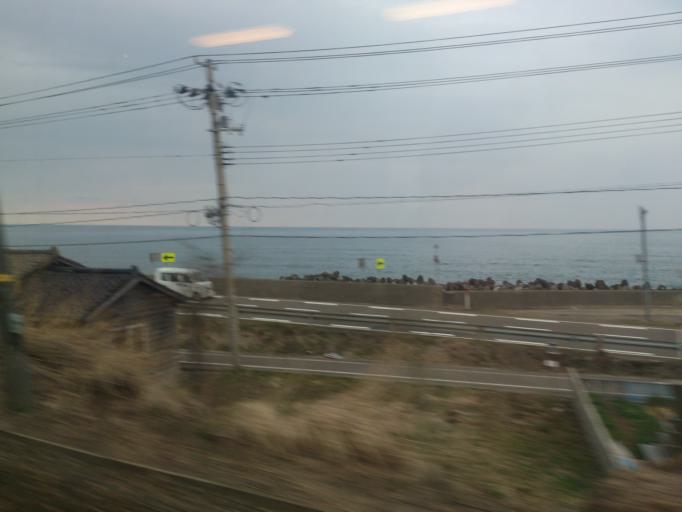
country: JP
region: Niigata
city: Joetsu
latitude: 37.1615
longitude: 138.1628
